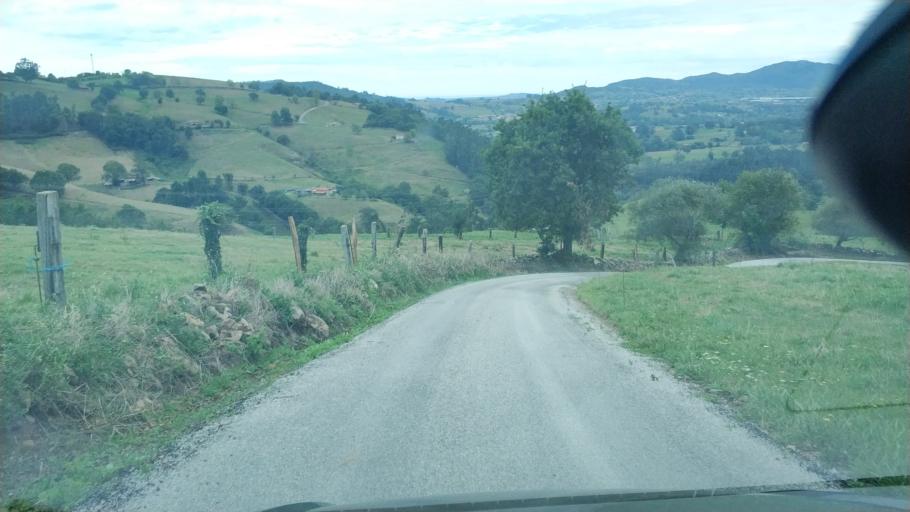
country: ES
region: Cantabria
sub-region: Provincia de Cantabria
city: Santa Maria de Cayon
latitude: 43.2898
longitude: -3.8547
